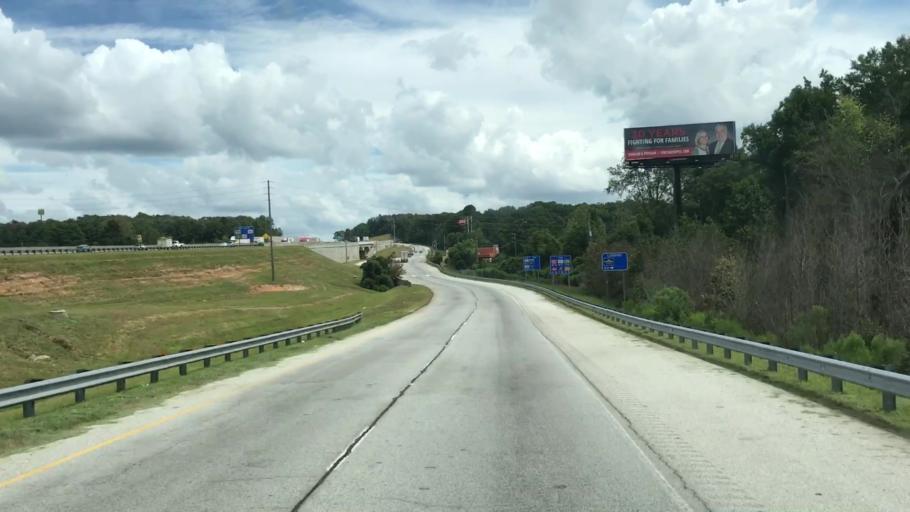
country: US
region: Georgia
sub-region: DeKalb County
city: Lithonia
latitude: 33.7014
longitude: -84.1213
